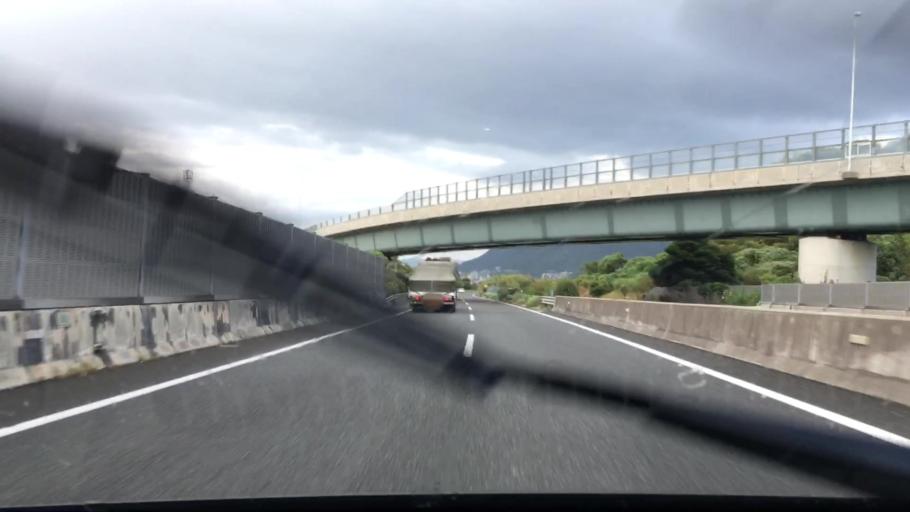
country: JP
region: Fukuoka
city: Kitakyushu
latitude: 33.8165
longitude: 130.8850
